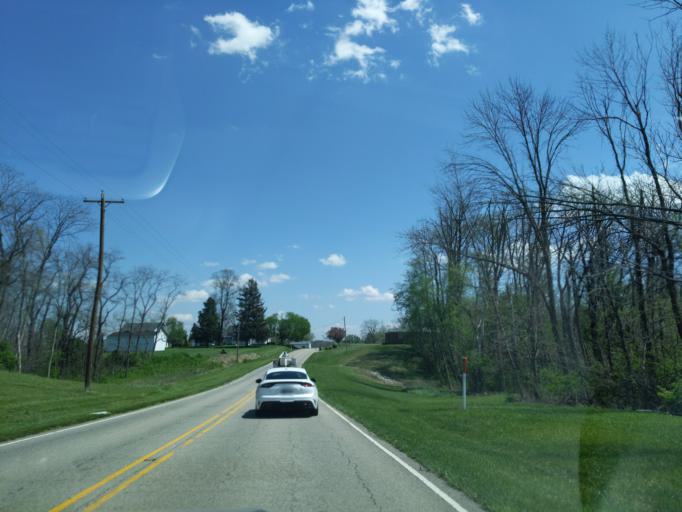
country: US
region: Indiana
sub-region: Decatur County
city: Saint Paul
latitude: 39.4052
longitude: -85.5646
